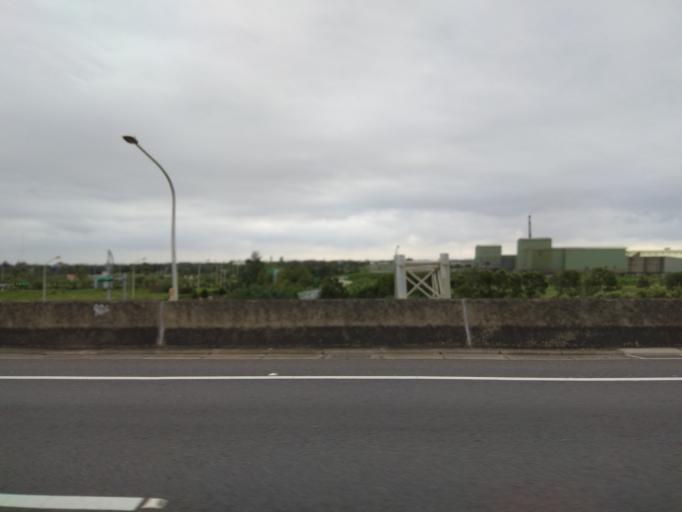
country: TW
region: Taiwan
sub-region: Hsinchu
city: Zhubei
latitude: 25.0461
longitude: 121.0797
